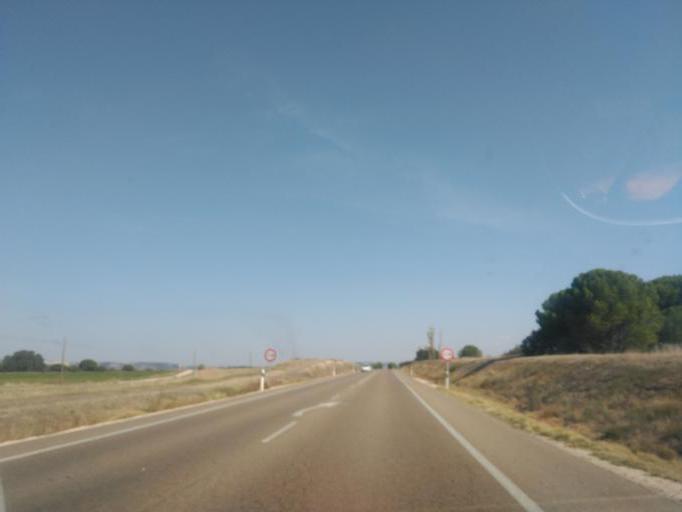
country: ES
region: Castille and Leon
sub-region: Provincia de Valladolid
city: Quintanilla de Arriba
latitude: 41.6157
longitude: -4.1926
